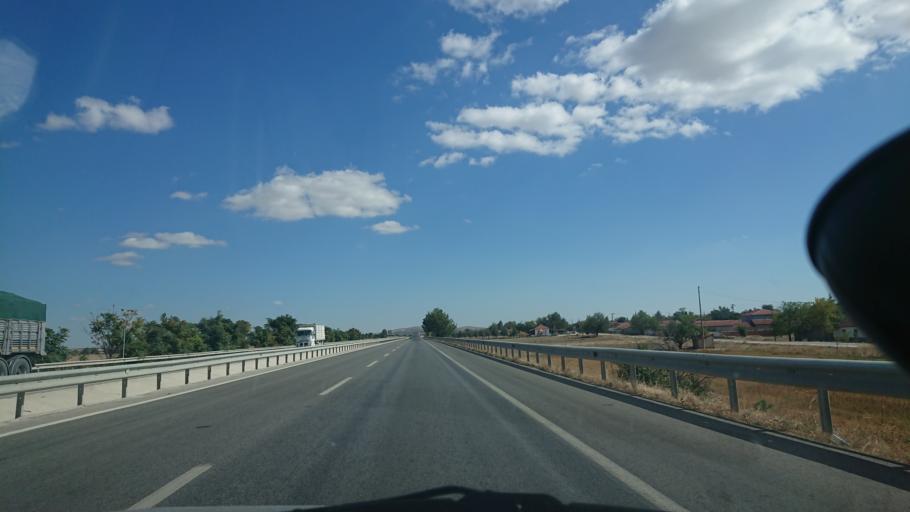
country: TR
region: Eskisehir
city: Mahmudiye
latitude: 39.5424
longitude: 30.9367
